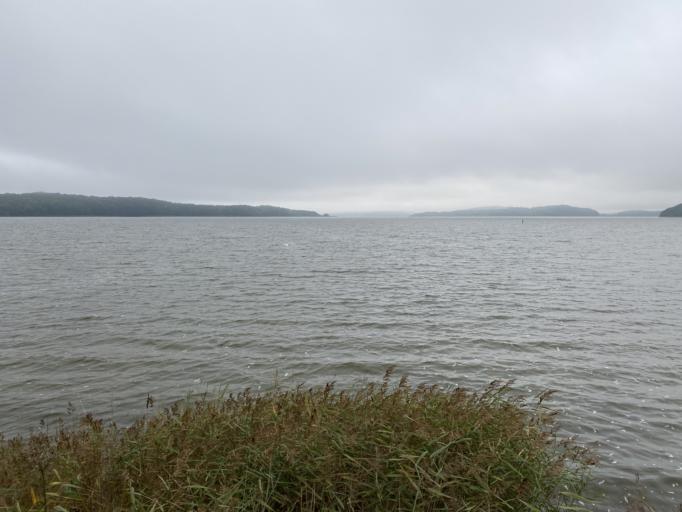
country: DE
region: Mecklenburg-Vorpommern
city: Ostseebad Binz
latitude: 54.4430
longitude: 13.5561
